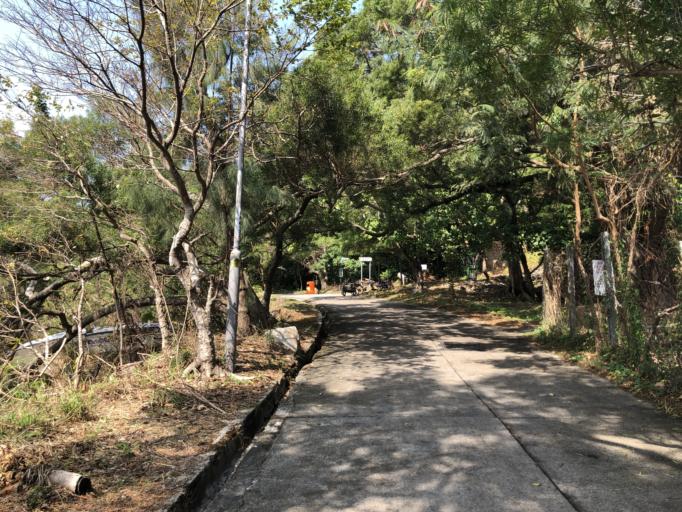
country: HK
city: Yung Shue Wan
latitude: 22.2180
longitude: 114.0267
